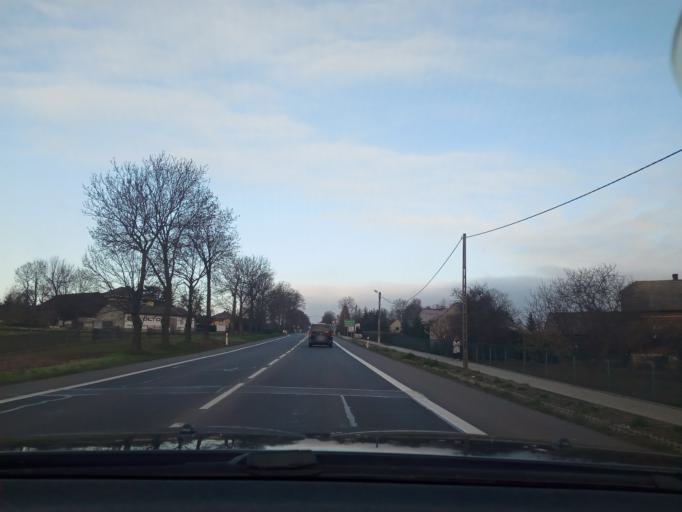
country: PL
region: Lesser Poland Voivodeship
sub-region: Powiat krakowski
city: Slomniki
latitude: 50.2669
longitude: 20.0740
